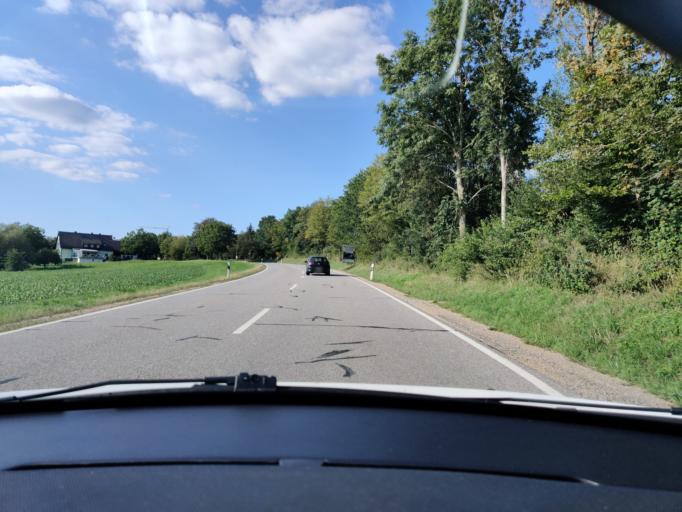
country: DE
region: Bavaria
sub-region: Upper Palatinate
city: Schwarzenfeld
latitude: 49.3836
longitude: 12.1563
